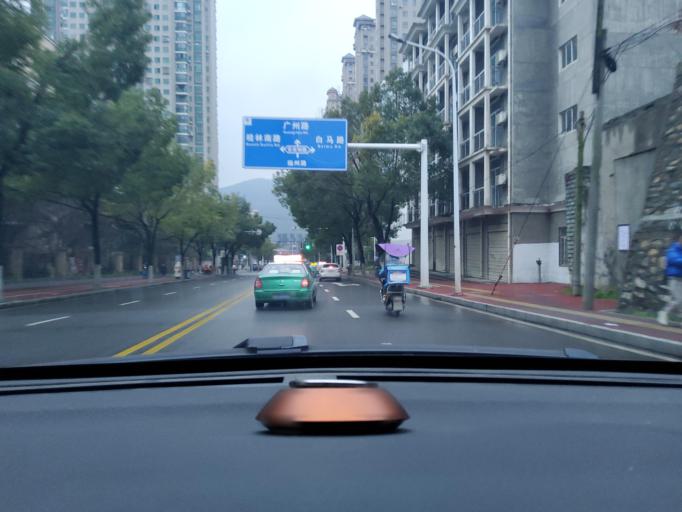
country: CN
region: Hubei
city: Tuanchengshan
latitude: 30.1903
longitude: 115.0275
